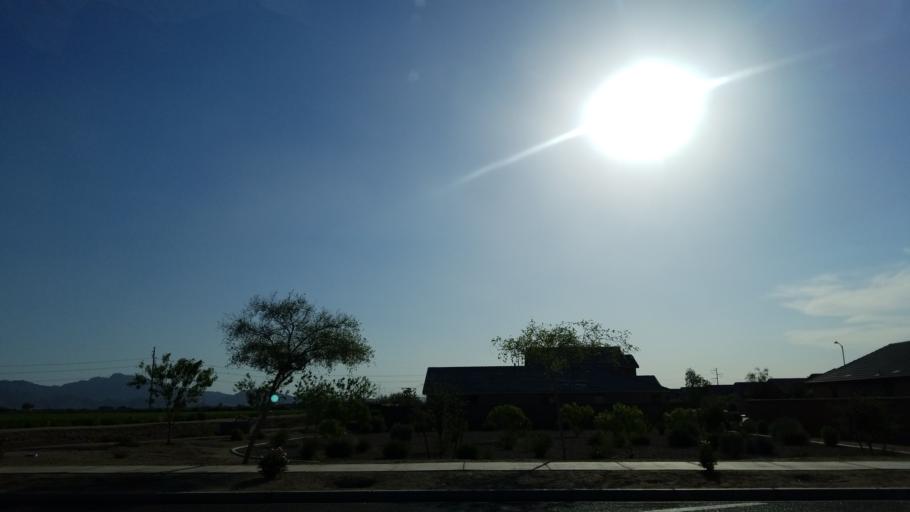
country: US
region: Arizona
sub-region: Maricopa County
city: Laveen
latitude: 33.3813
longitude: -112.2198
